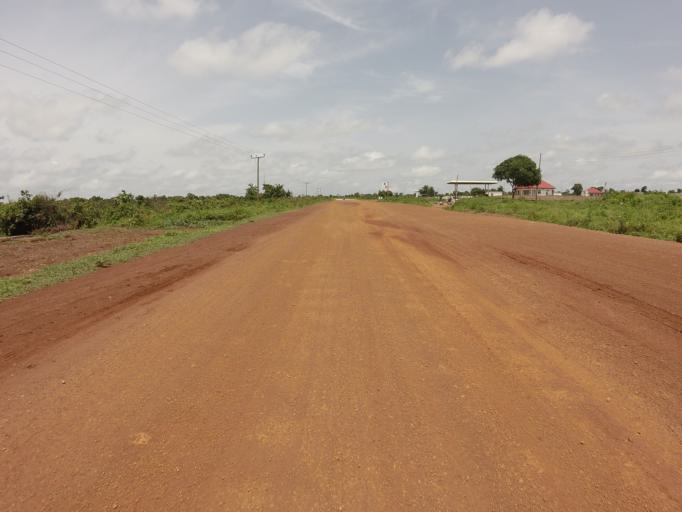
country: GH
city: Kpandae
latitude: 8.5853
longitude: 0.2386
